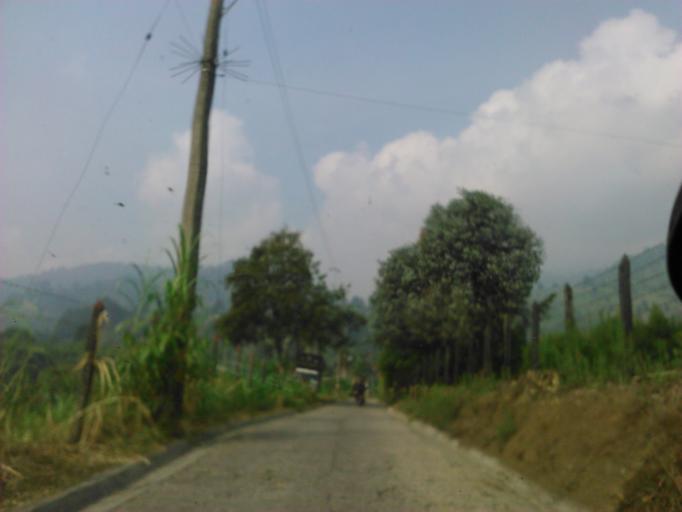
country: CO
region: Antioquia
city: La Estrella
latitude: 6.1421
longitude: -75.6425
